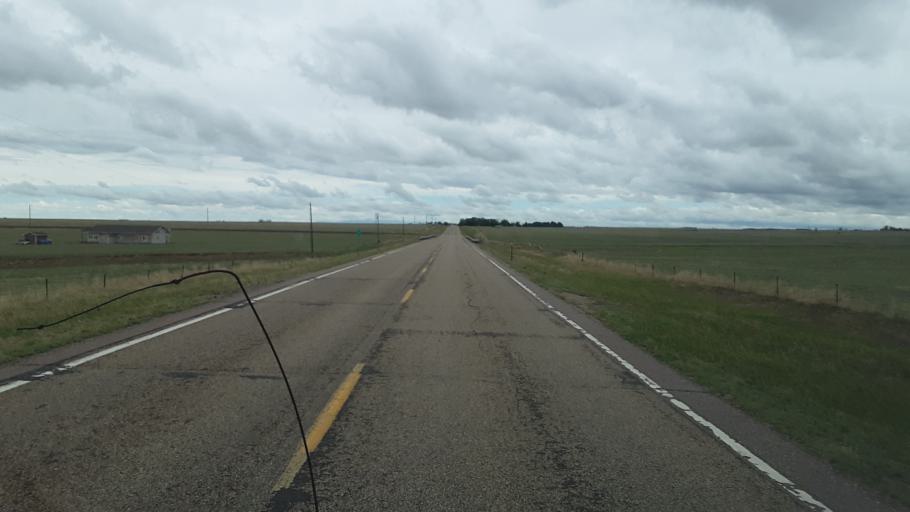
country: US
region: Colorado
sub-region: El Paso County
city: Ellicott
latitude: 38.8398
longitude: -104.0362
